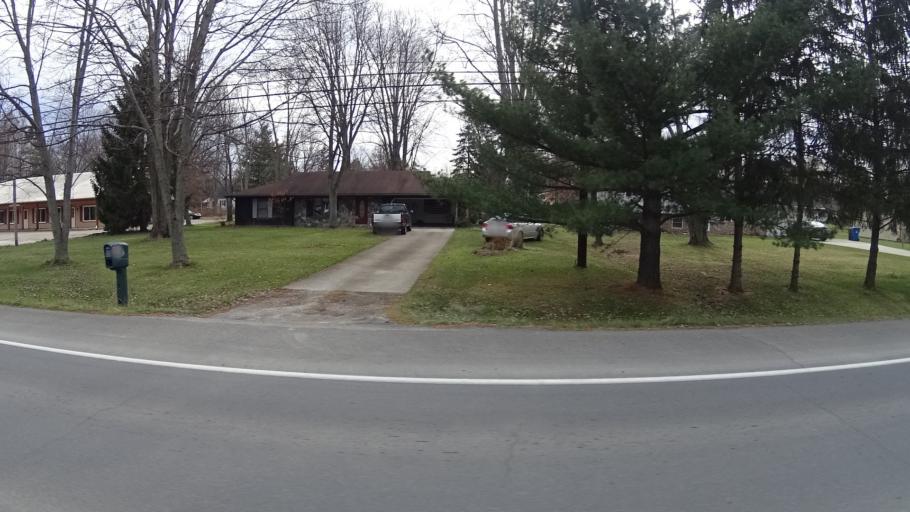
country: US
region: Ohio
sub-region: Lorain County
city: Eaton Estates
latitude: 41.3131
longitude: -81.9489
